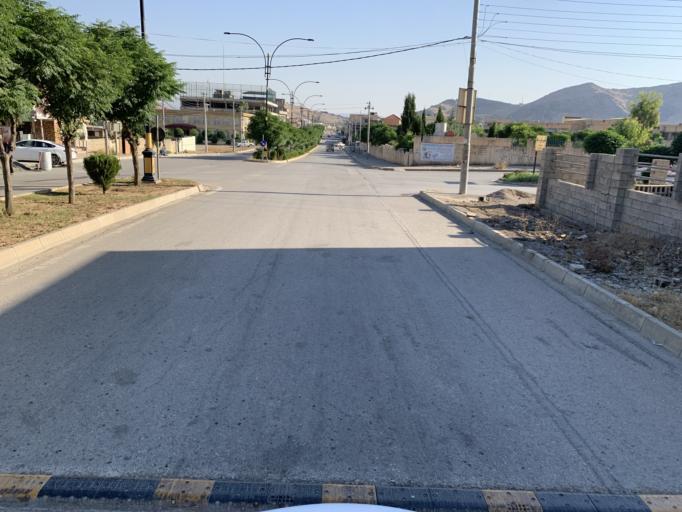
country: IQ
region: As Sulaymaniyah
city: Raniye
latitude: 36.2452
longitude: 44.8738
